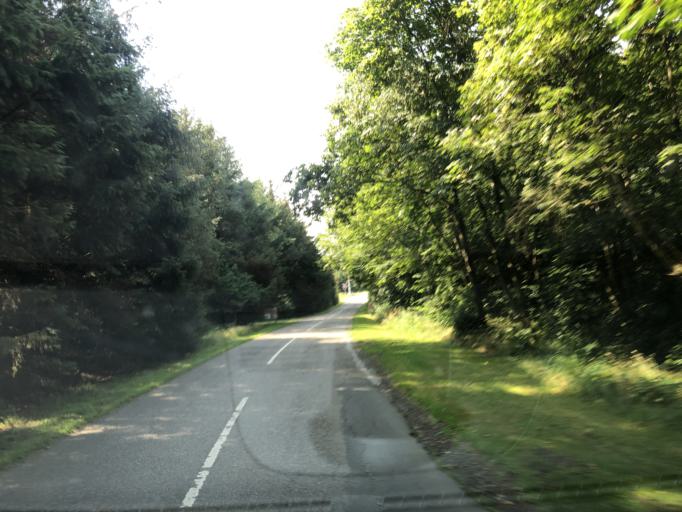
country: DK
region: Central Jutland
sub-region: Lemvig Kommune
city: Lemvig
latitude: 56.4387
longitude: 8.2856
